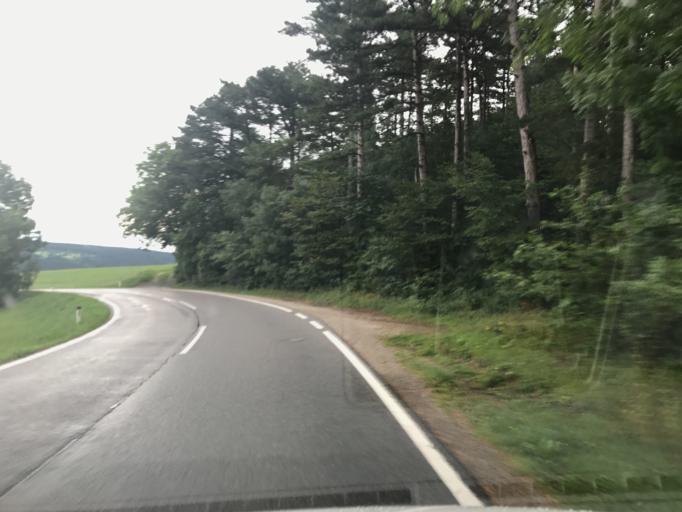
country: AT
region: Lower Austria
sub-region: Politischer Bezirk Wiener Neustadt
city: Markt Piesting
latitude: 47.8656
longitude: 16.1032
